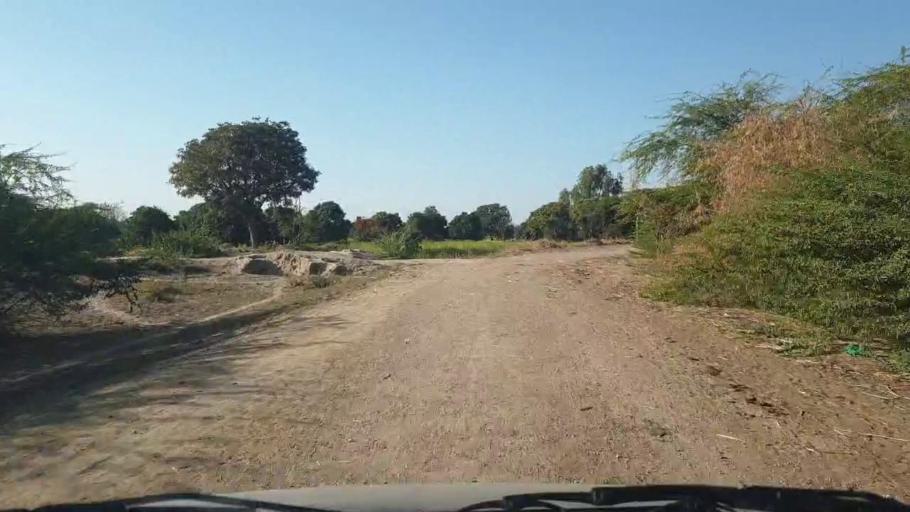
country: PK
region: Sindh
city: Samaro
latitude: 25.3656
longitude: 69.2906
